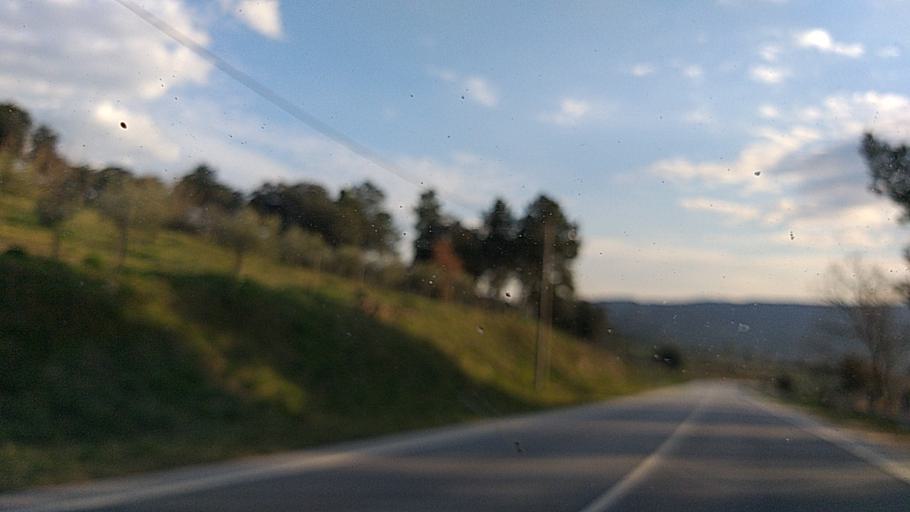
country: ES
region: Castille and Leon
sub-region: Provincia de Salamanca
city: Aldea del Obispo
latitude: 40.7043
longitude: -6.9261
